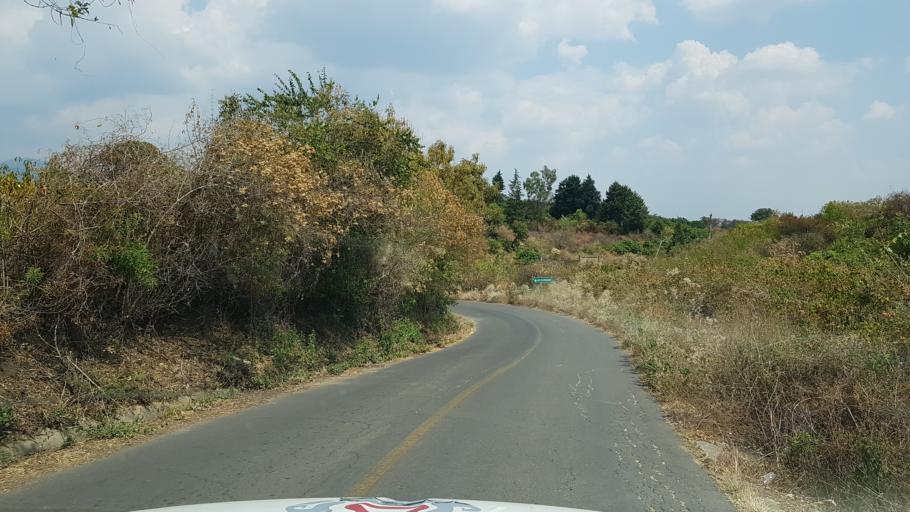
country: MX
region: Morelos
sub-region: Yecapixtla
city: Texcala
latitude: 18.9196
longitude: -98.8112
